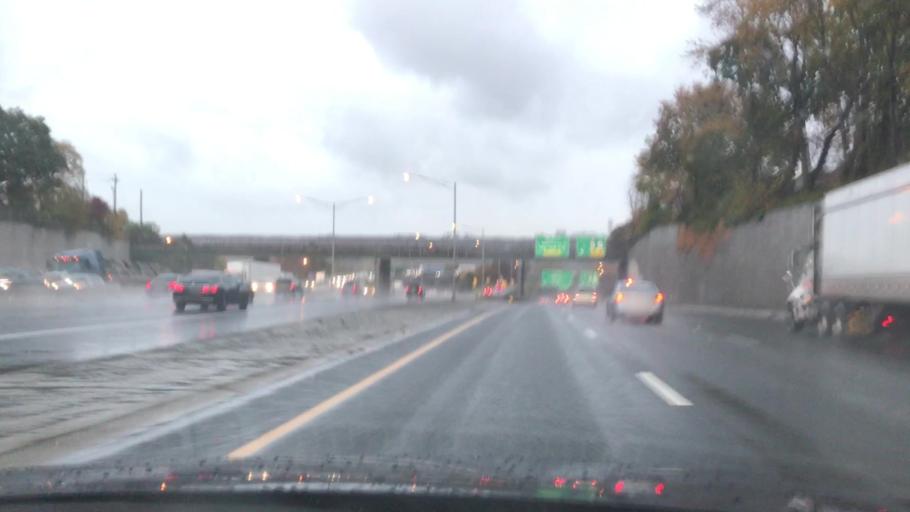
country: US
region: New Jersey
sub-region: Bergen County
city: Ridgefield Park
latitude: 40.8652
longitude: -74.0176
